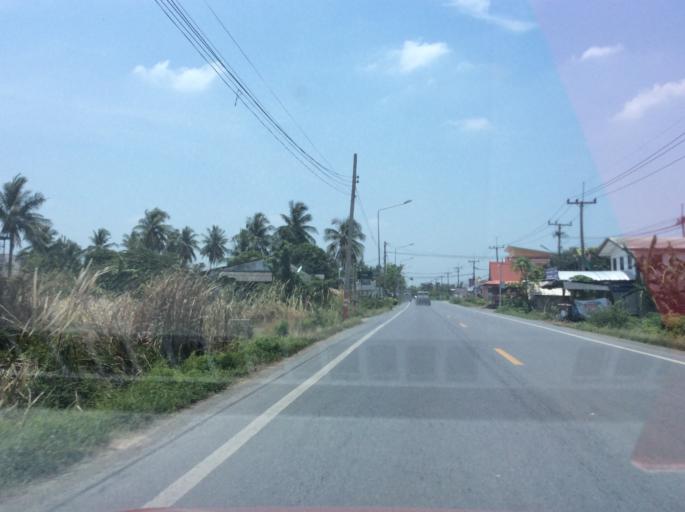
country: TH
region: Pathum Thani
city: Ban Lam Luk Ka
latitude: 13.9887
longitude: 100.7777
